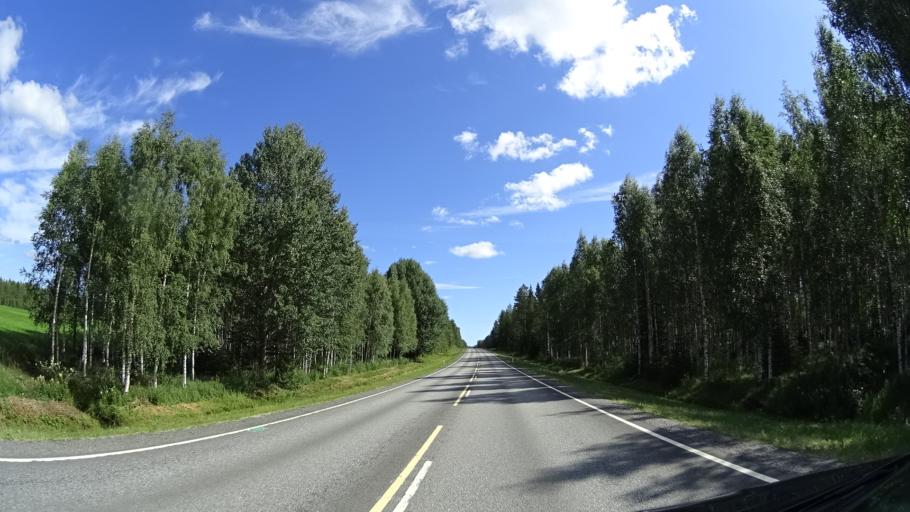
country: FI
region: Pirkanmaa
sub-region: Luoteis-Pirkanmaa
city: Kihnioe
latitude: 62.2034
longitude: 23.2230
